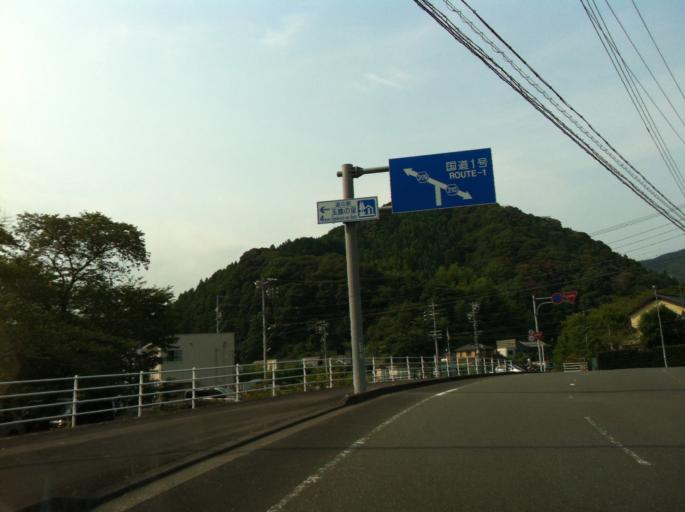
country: JP
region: Shizuoka
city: Fujieda
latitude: 34.9277
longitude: 138.2717
